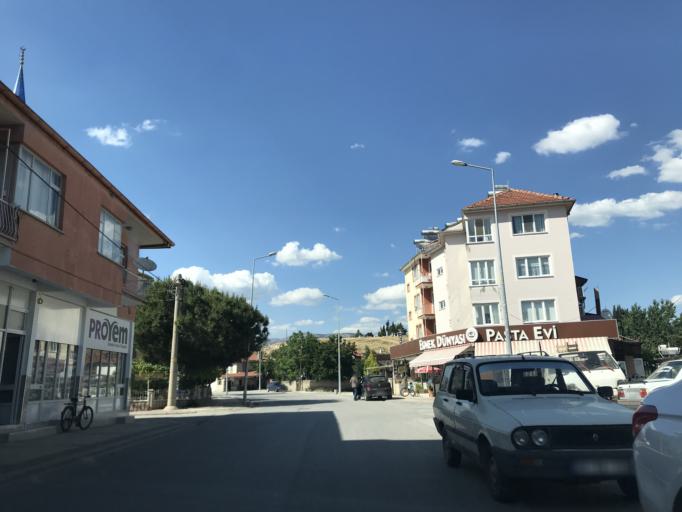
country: TR
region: Denizli
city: Civril
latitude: 38.3039
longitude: 29.7409
